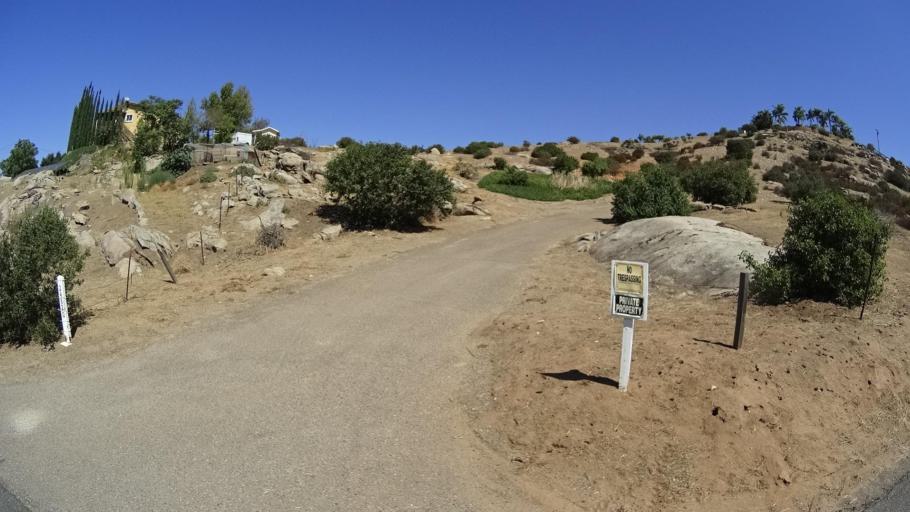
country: US
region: California
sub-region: San Diego County
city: San Diego Country Estates
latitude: 33.0495
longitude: -116.7937
